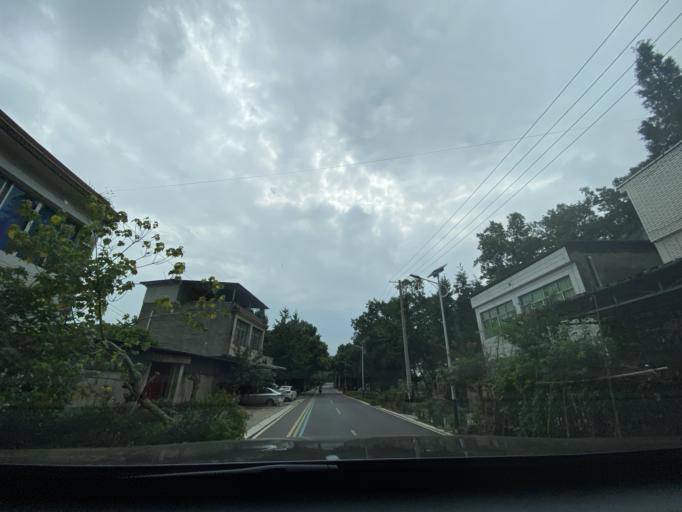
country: CN
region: Sichuan
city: Wujin
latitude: 30.4010
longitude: 103.9871
